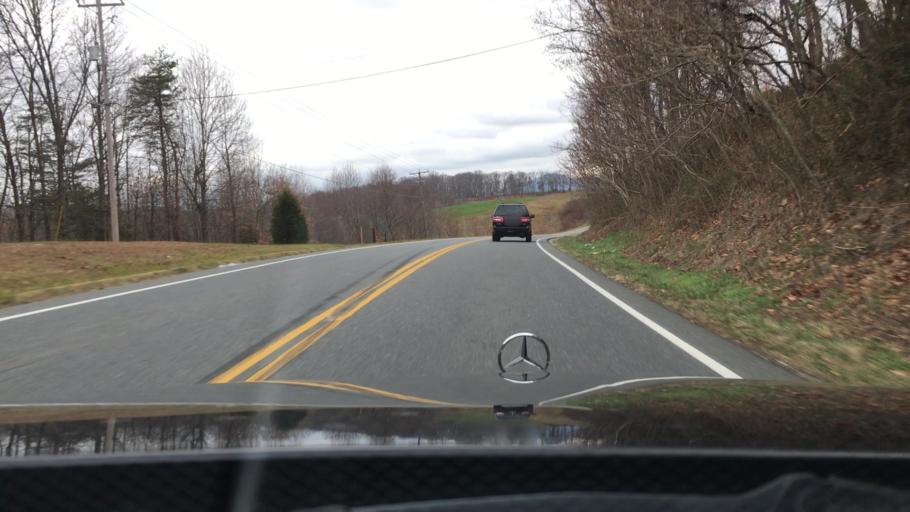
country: US
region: Virginia
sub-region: Franklin County
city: North Shore
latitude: 37.2441
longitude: -79.6803
